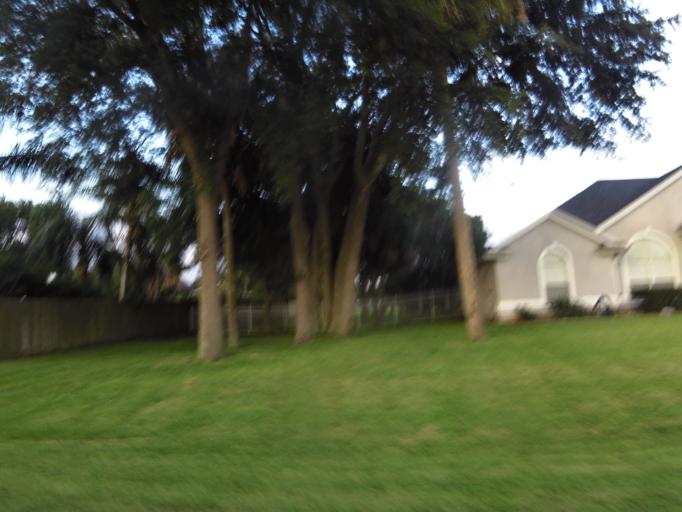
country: US
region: Florida
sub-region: Duval County
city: Atlantic Beach
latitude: 30.3969
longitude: -81.4964
